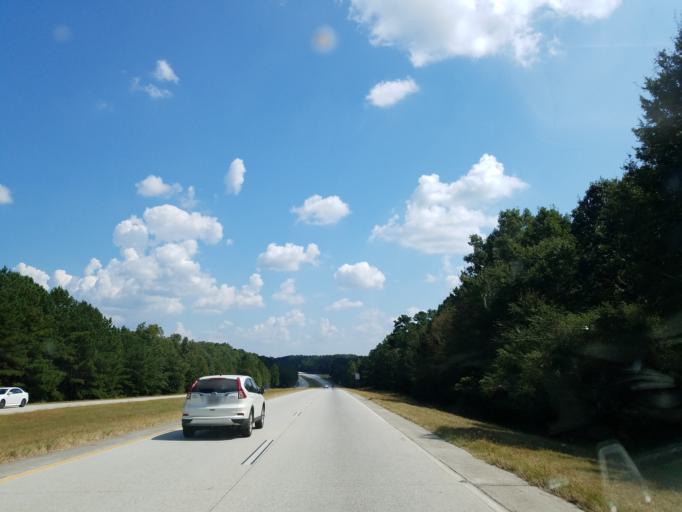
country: US
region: Georgia
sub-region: Barrow County
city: Statham
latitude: 33.9501
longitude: -83.5895
